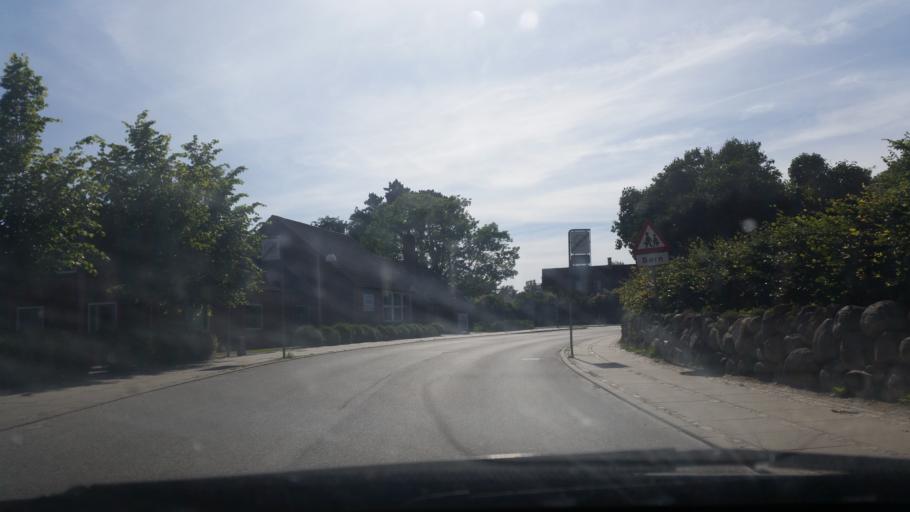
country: DK
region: Central Jutland
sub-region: Samso Kommune
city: Tranebjerg
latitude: 55.8334
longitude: 10.5885
